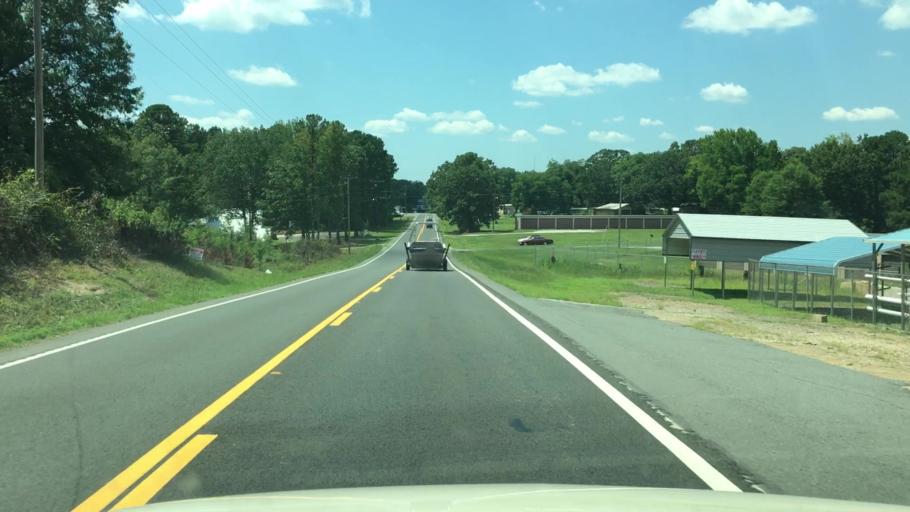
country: US
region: Arkansas
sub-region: Garland County
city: Lake Hamilton
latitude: 34.2665
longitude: -93.1395
